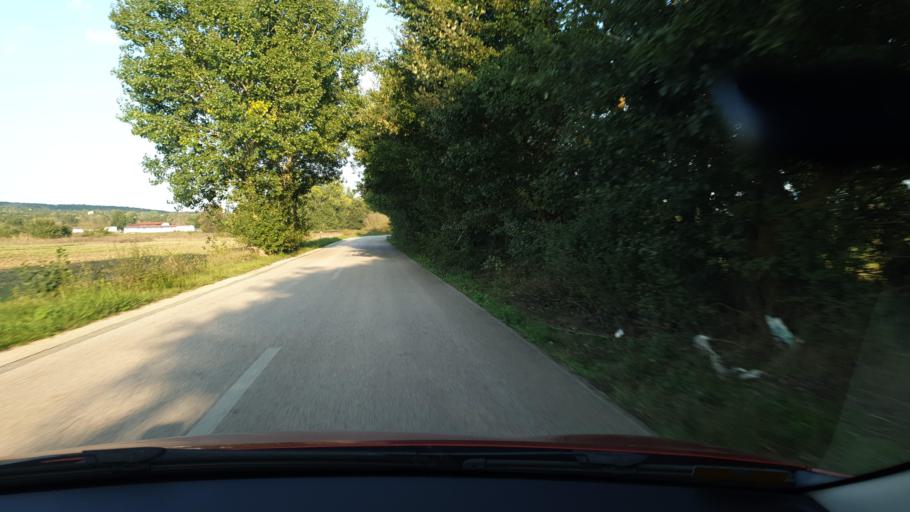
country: GR
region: Central Macedonia
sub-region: Nomos Chalkidikis
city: Galatista
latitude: 40.5643
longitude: 23.3320
